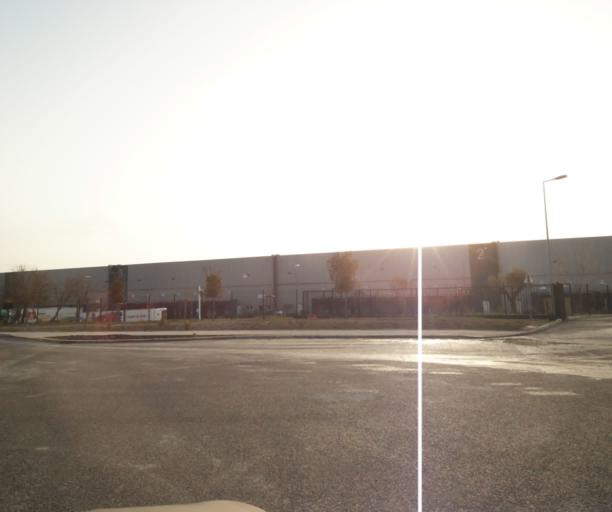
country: FR
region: Provence-Alpes-Cote d'Azur
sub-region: Departement des Bouches-du-Rhone
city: Rousset
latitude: 43.4659
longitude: 5.6012
